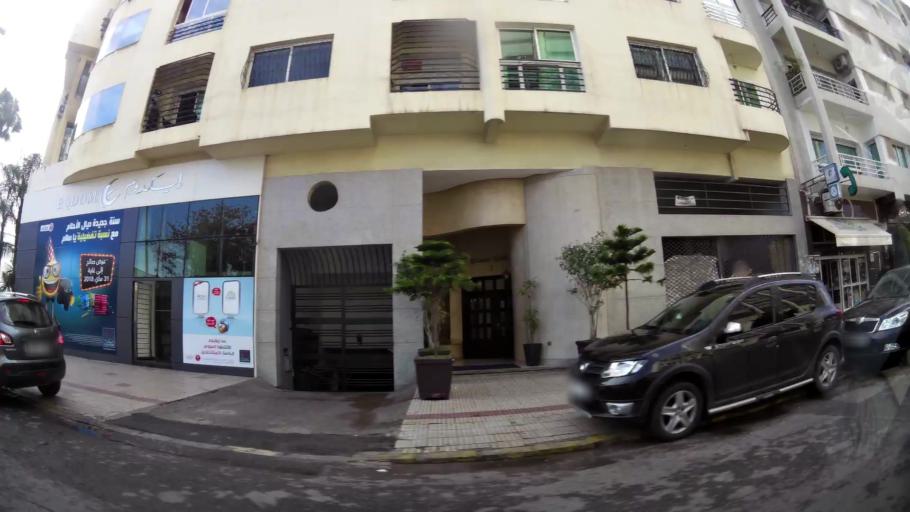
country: MA
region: Grand Casablanca
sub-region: Casablanca
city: Casablanca
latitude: 33.5842
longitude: -7.6280
